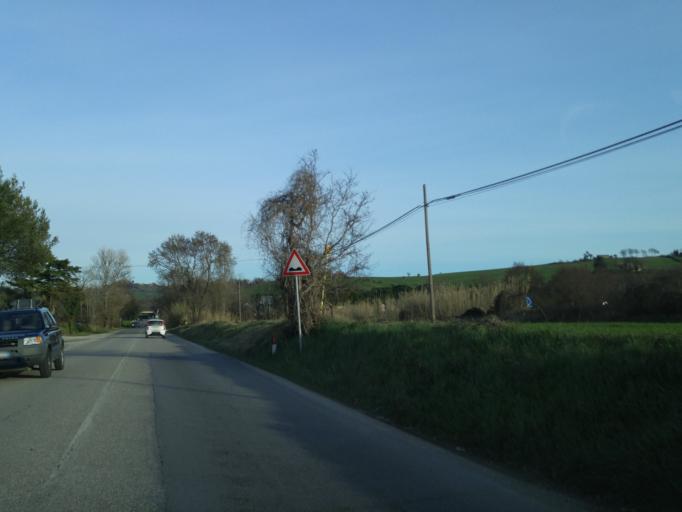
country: IT
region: The Marches
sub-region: Provincia di Pesaro e Urbino
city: Fossombrone
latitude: 43.6887
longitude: 12.8353
